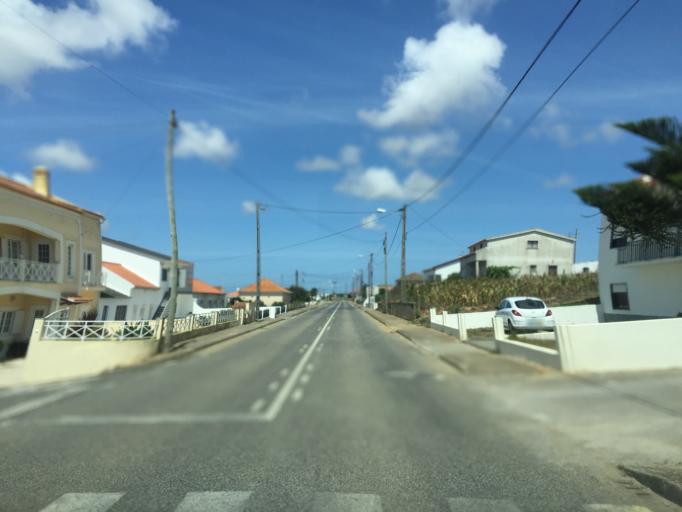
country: PT
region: Lisbon
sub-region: Lourinha
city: Lourinha
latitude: 39.2824
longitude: -9.3019
